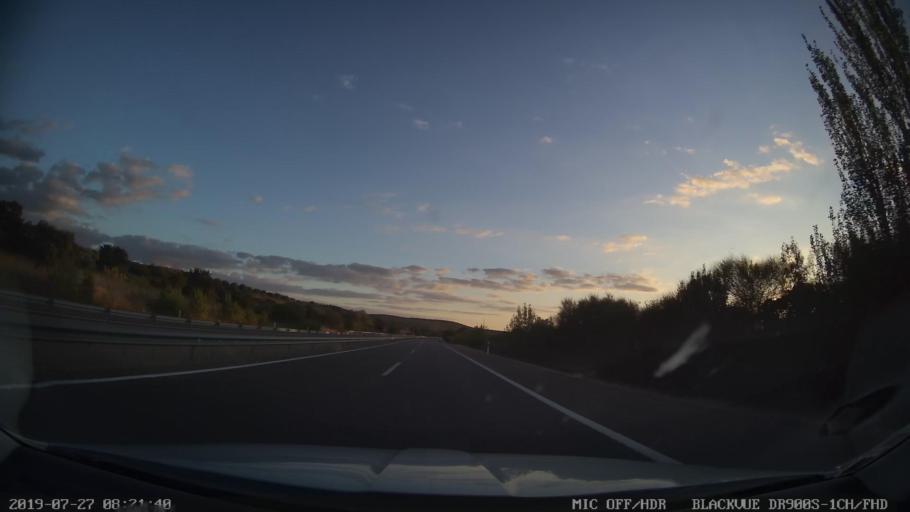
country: ES
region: Extremadura
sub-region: Provincia de Badajoz
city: Torremayor
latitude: 38.8620
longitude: -6.5292
